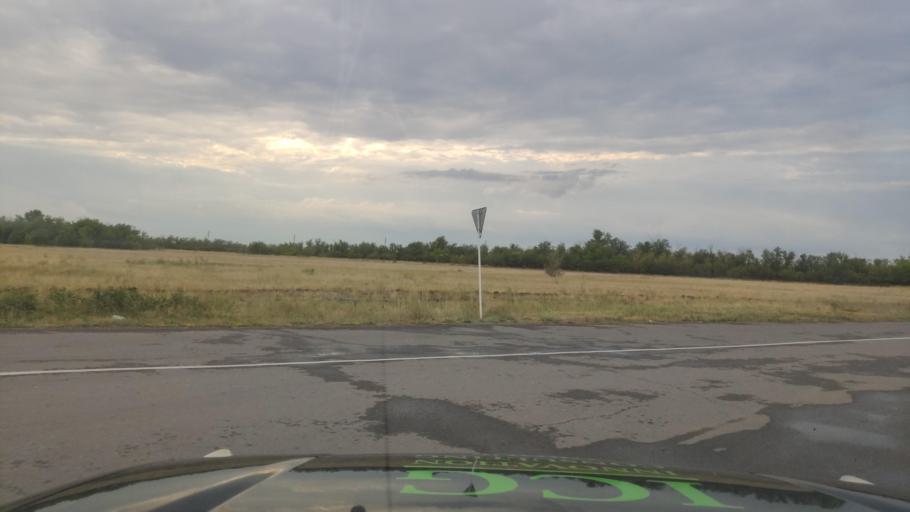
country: KZ
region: Pavlodar
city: Pavlodar
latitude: 52.3421
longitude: 77.2492
